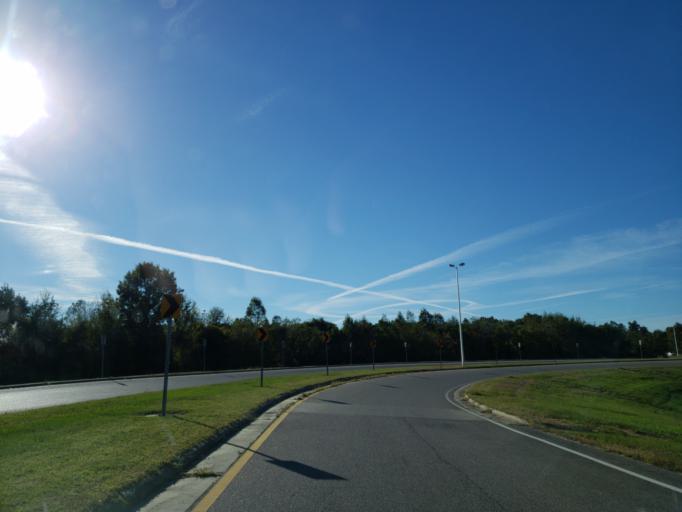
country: US
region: Mississippi
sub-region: Forrest County
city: Petal
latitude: 31.3580
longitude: -89.2740
